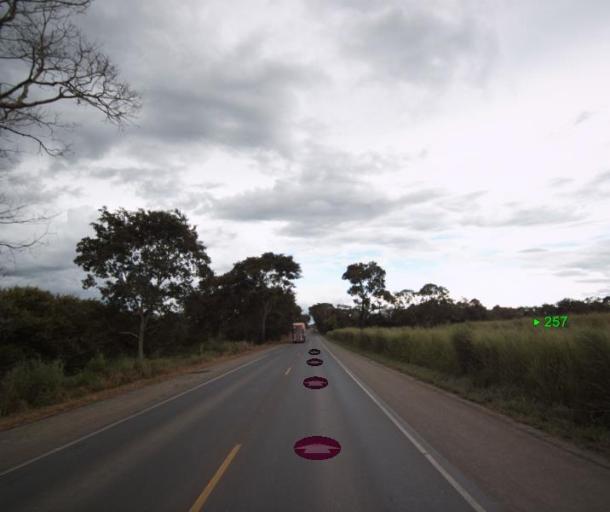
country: BR
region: Goias
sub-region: Itapaci
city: Itapaci
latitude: -14.9753
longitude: -49.3936
